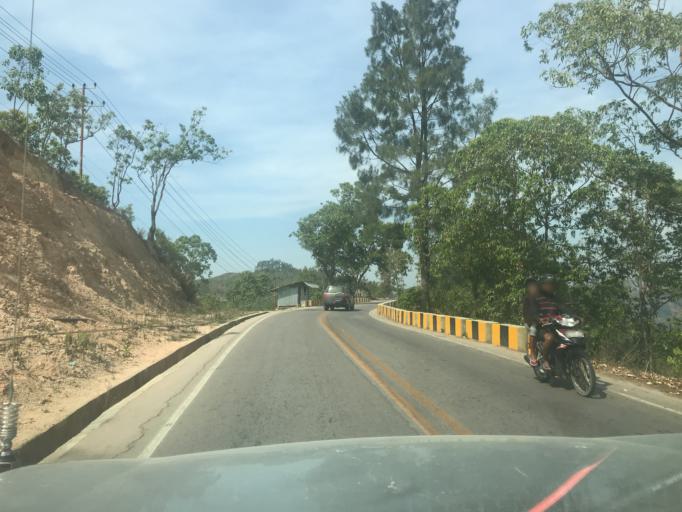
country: TL
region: Aileu
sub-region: Aileu Villa
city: Aileu
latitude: -8.6820
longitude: 125.5508
